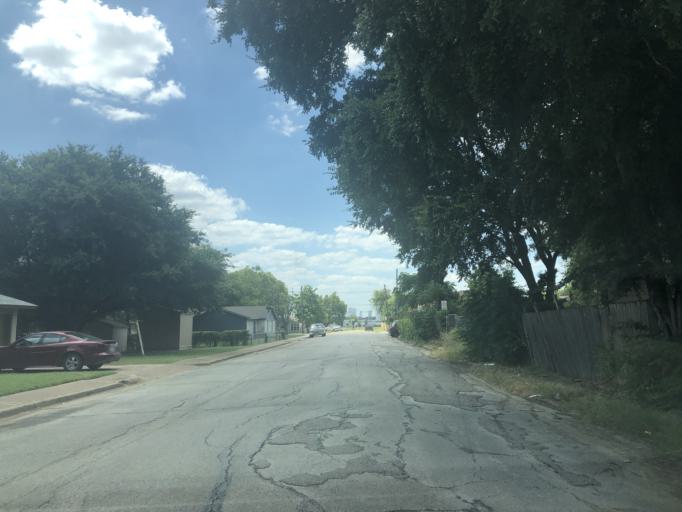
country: US
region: Texas
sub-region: Dallas County
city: Grand Prairie
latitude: 32.7341
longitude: -97.0327
